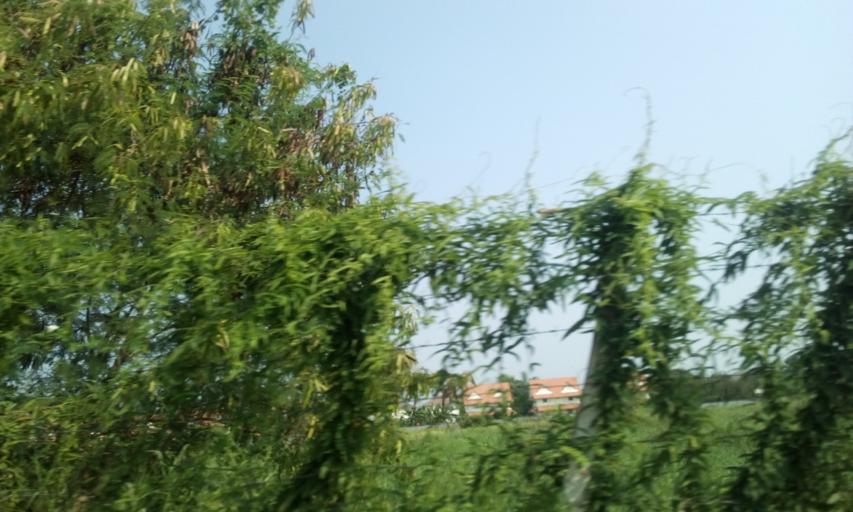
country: TH
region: Pathum Thani
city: Ban Rangsit
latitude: 14.0185
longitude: 100.7591
